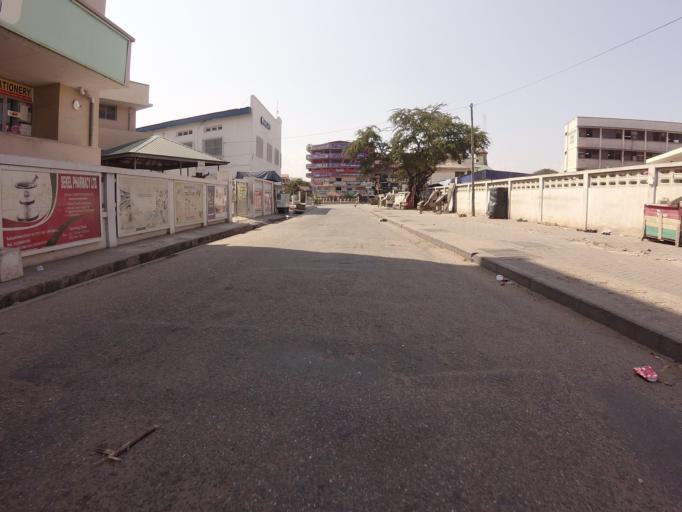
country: GH
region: Greater Accra
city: Accra
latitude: 5.5451
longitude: -0.2062
